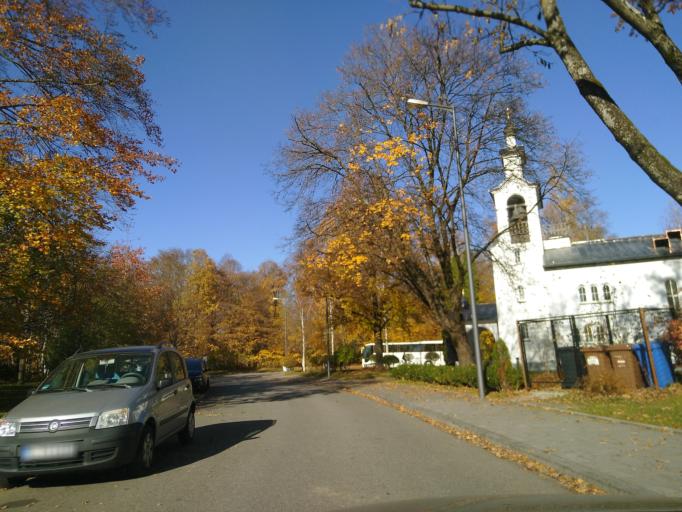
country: DE
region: Bavaria
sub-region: Upper Bavaria
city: Unterhaching
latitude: 48.0952
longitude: 11.5956
